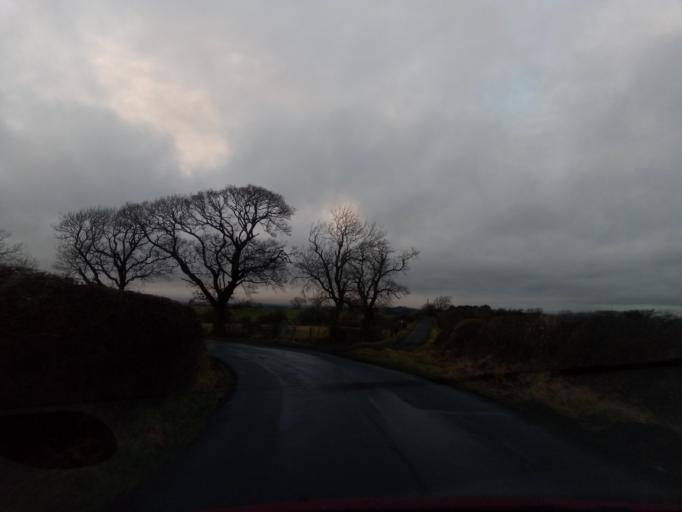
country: GB
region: England
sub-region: Northumberland
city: Meldon
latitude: 55.1428
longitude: -1.8154
